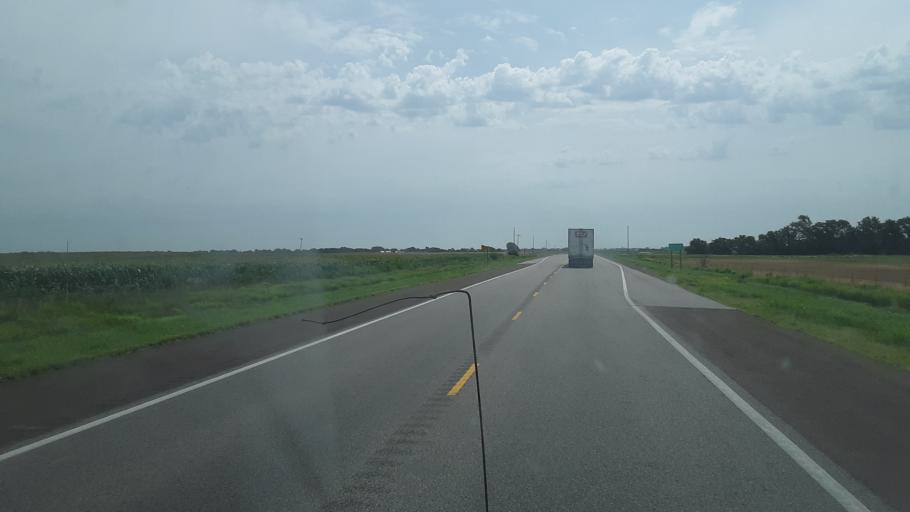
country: US
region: Kansas
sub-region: Reno County
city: South Hutchinson
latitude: 37.9850
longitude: -98.0904
